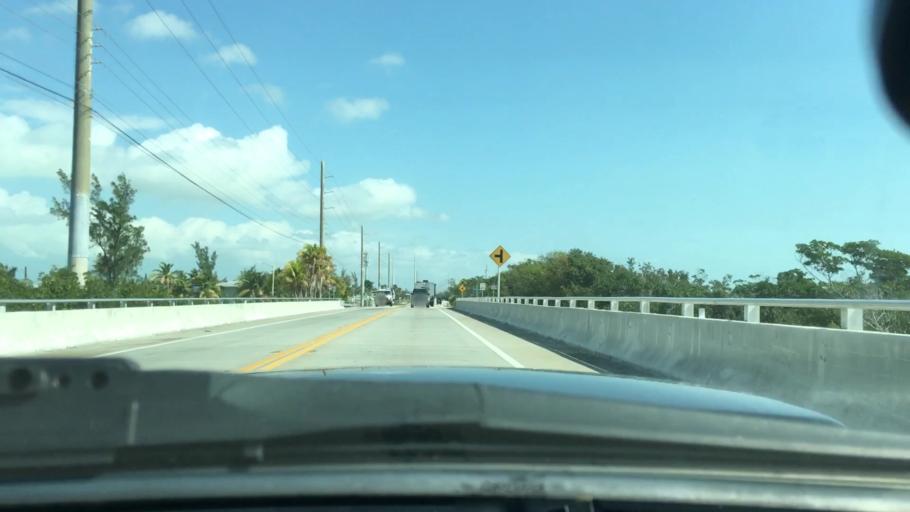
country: US
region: Florida
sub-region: Monroe County
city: Big Coppitt Key
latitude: 24.5928
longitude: -81.6660
